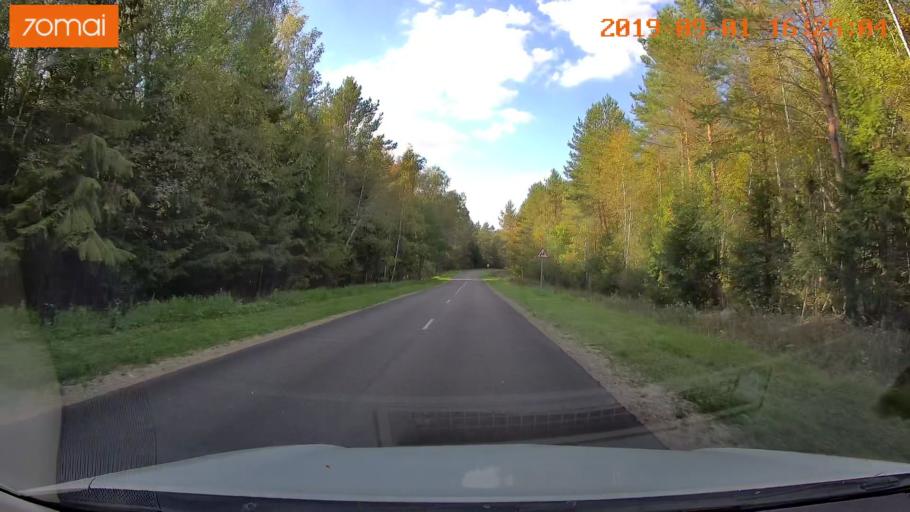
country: RU
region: Kaluga
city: Maloyaroslavets
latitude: 54.8985
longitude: 36.5179
